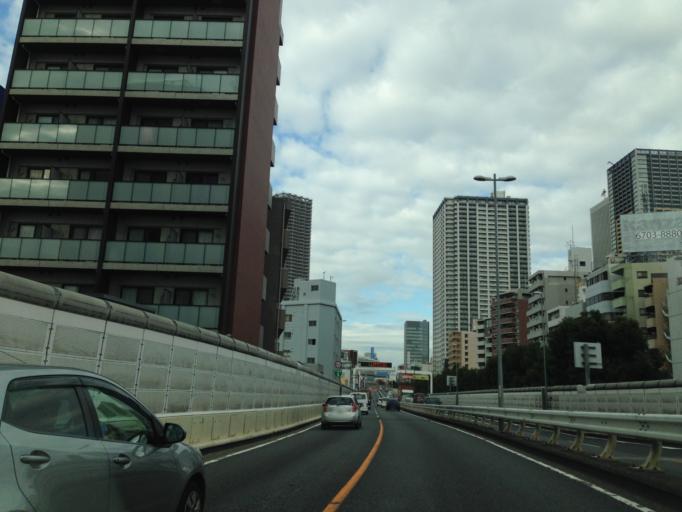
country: JP
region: Tokyo
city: Tokyo
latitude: 35.7236
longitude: 139.7223
